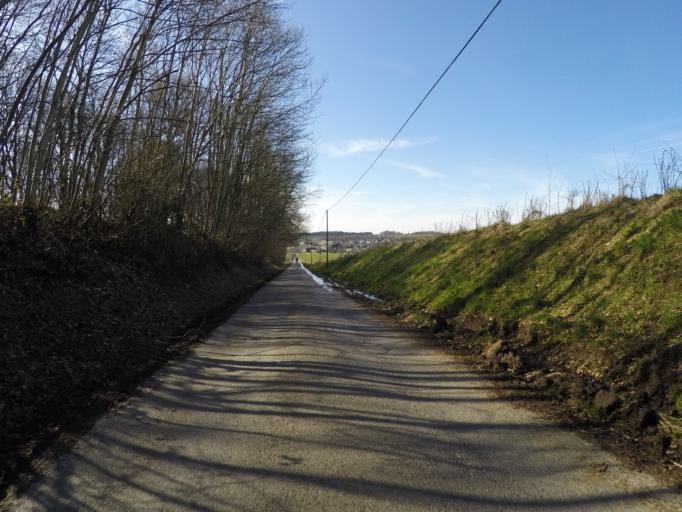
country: BE
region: Wallonia
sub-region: Province de Namur
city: Hamois
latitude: 50.3438
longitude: 5.1298
